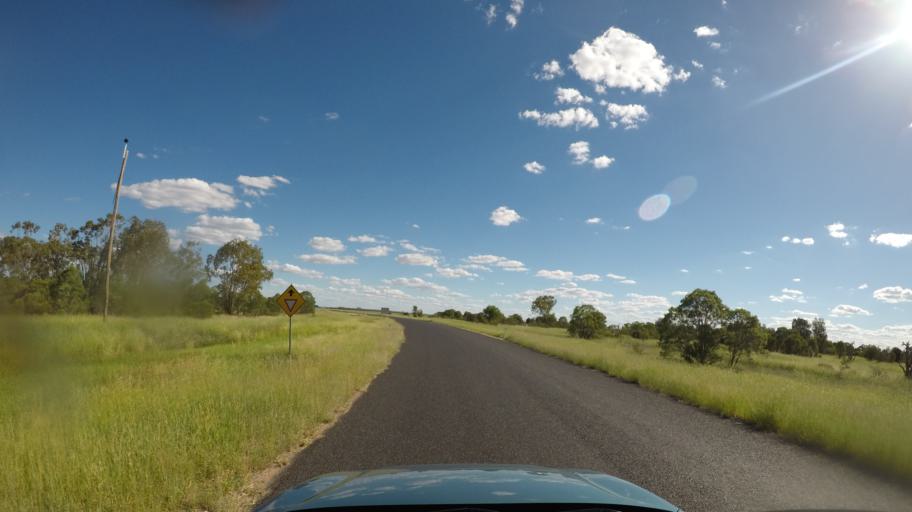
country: AU
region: Queensland
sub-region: Goondiwindi
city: Goondiwindi
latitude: -28.1782
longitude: 150.4680
